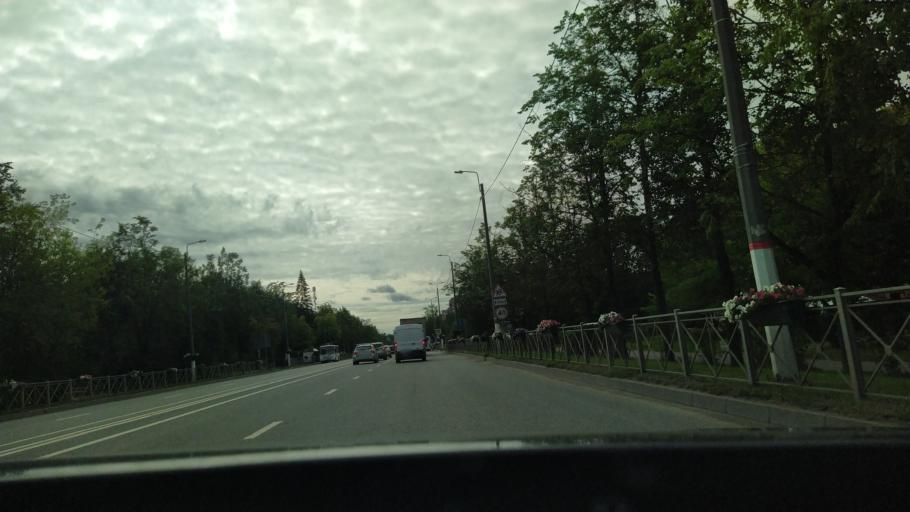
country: RU
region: Leningrad
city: Tosno
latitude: 59.5444
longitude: 30.8707
